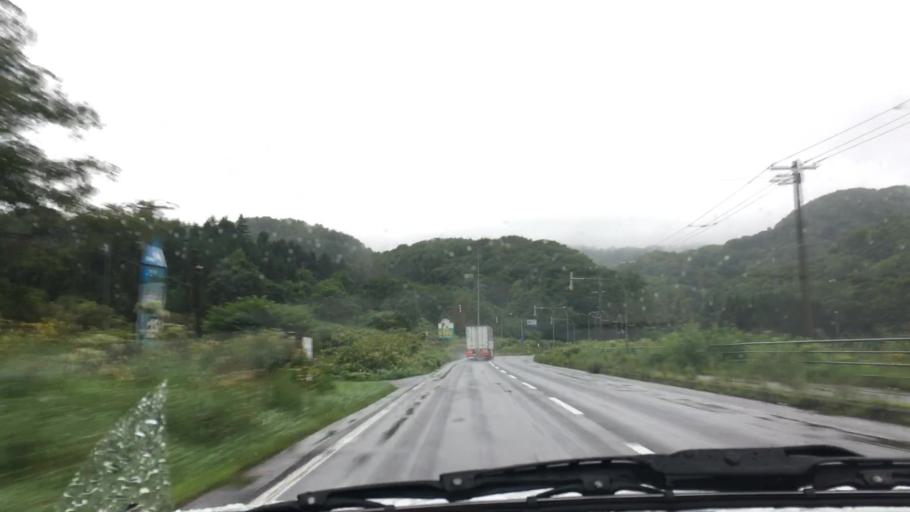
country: JP
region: Hokkaido
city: Niseko Town
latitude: 42.6007
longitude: 140.6239
